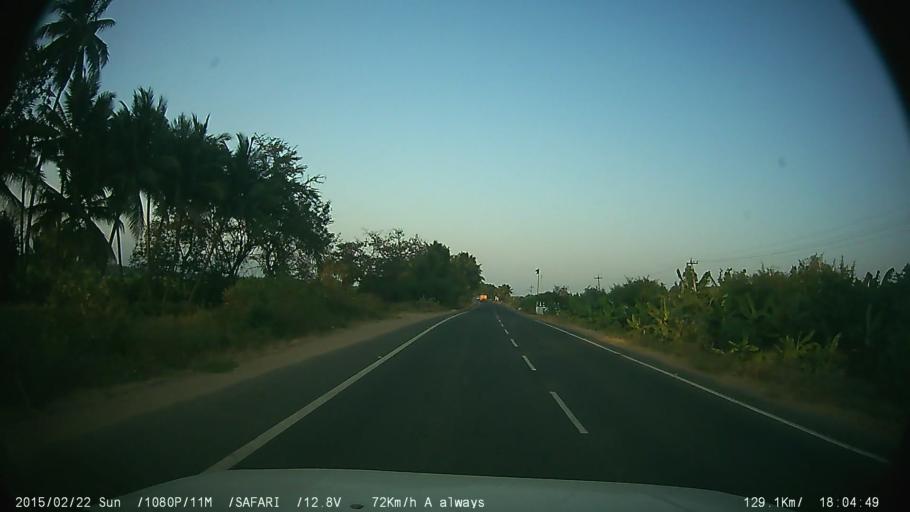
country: IN
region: Tamil Nadu
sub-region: Theni
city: Uttamapalaiyam
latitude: 9.8189
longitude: 77.3520
